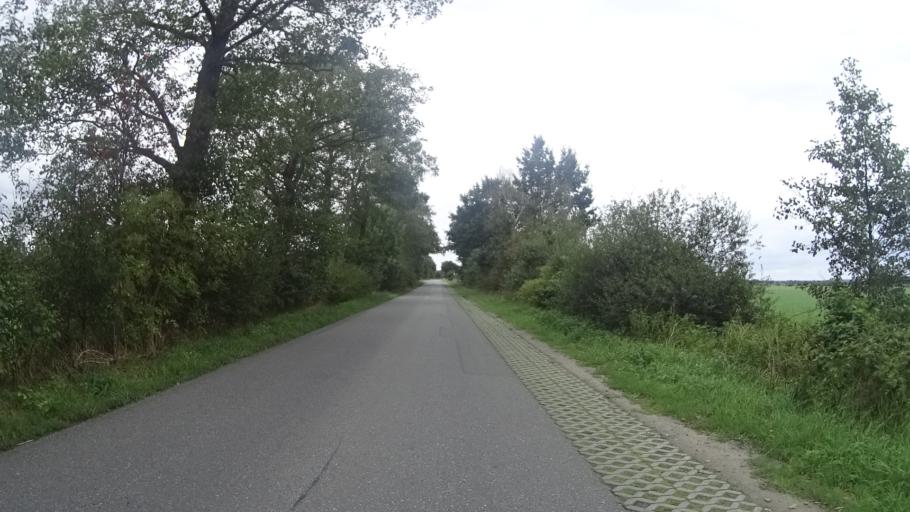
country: DE
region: Lower Saxony
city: Stinstedt
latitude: 53.6432
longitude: 8.9589
